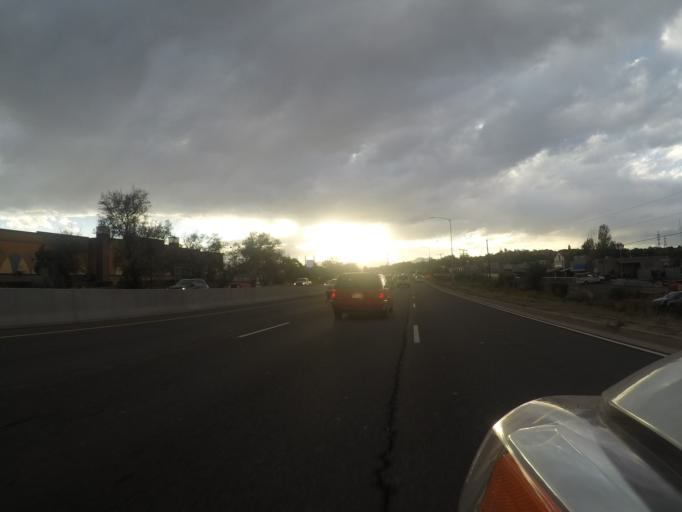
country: US
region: Colorado
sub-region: Arapahoe County
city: Sheridan
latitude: 39.6538
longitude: -105.0074
